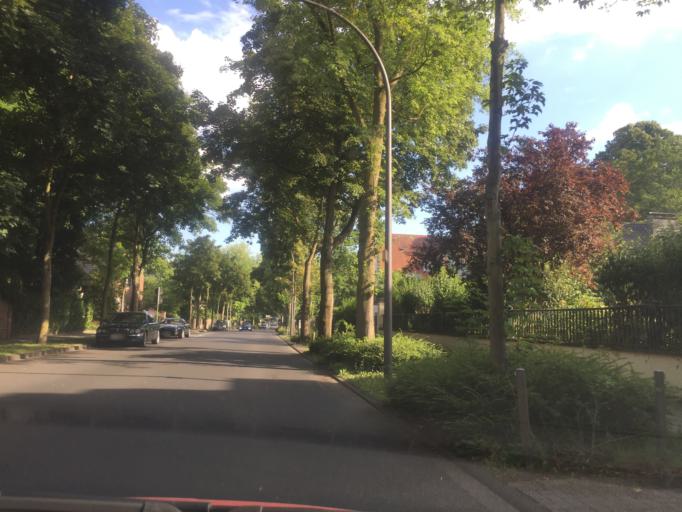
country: DE
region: North Rhine-Westphalia
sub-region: Regierungsbezirk Koln
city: Bayenthal
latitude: 50.9004
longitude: 6.9742
